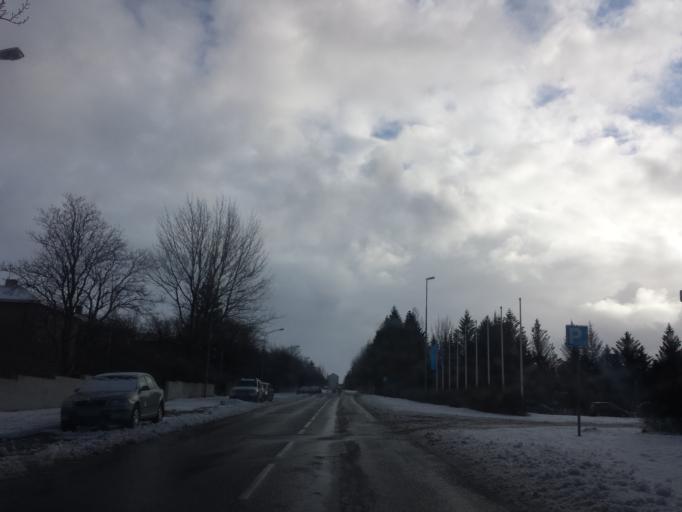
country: IS
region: Capital Region
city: Reykjavik
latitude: 64.1386
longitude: -21.9142
